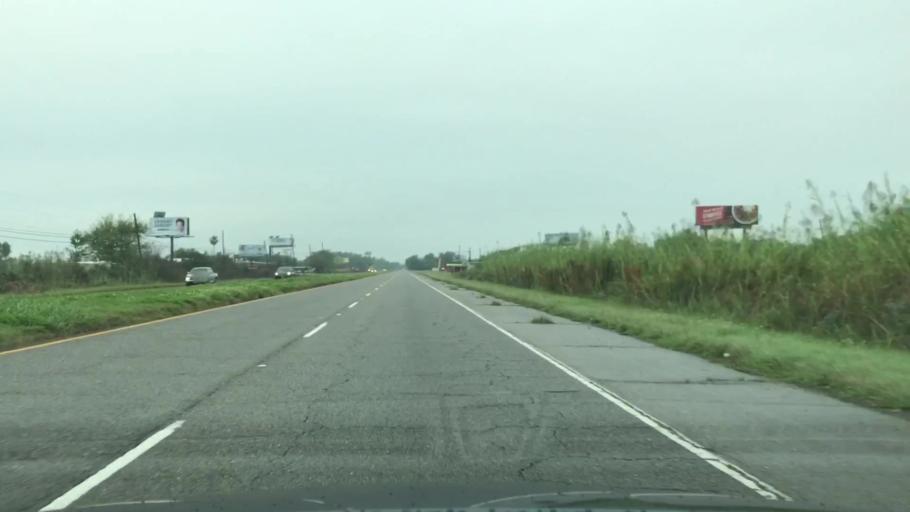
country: US
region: Louisiana
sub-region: Saint Charles Parish
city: Des Allemands
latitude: 29.8059
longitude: -90.4979
